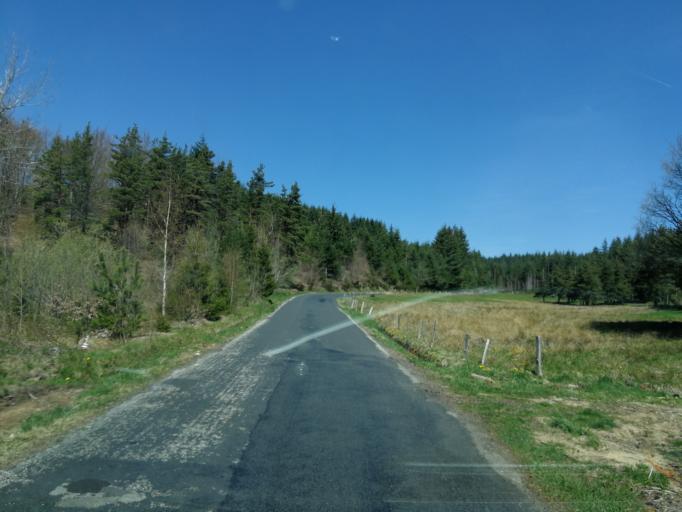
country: FR
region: Rhone-Alpes
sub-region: Departement de l'Ardeche
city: Le Cheylard
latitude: 44.9512
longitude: 4.4181
